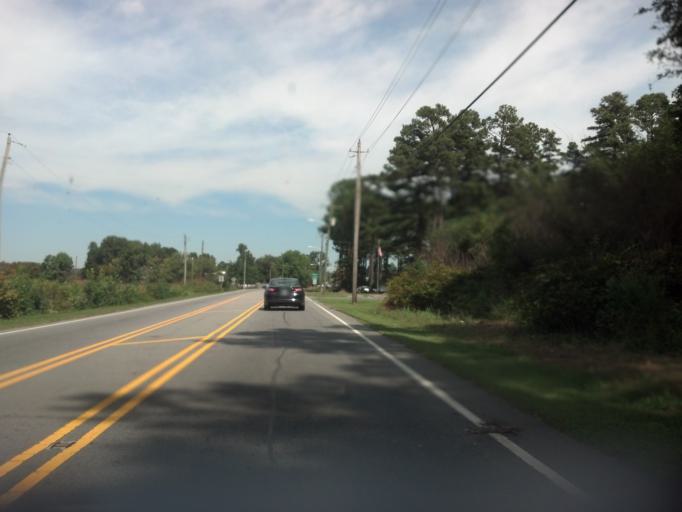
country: US
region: North Carolina
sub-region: Pitt County
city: Farmville
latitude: 35.5764
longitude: -77.5934
